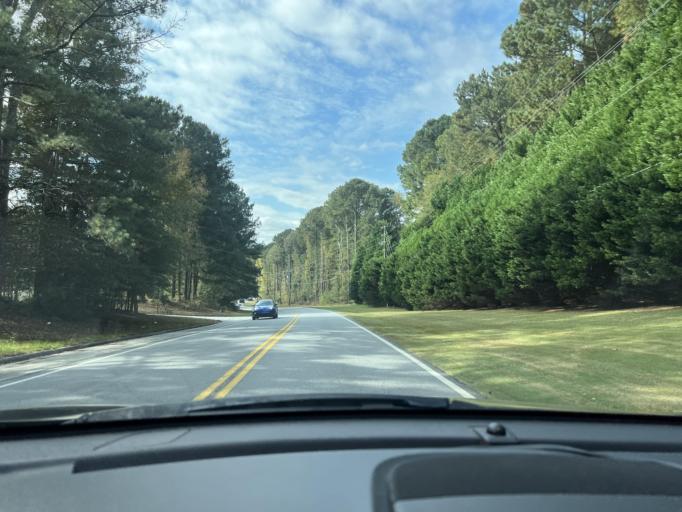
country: US
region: Georgia
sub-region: Gwinnett County
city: Grayson
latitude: 33.8986
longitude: -83.9838
